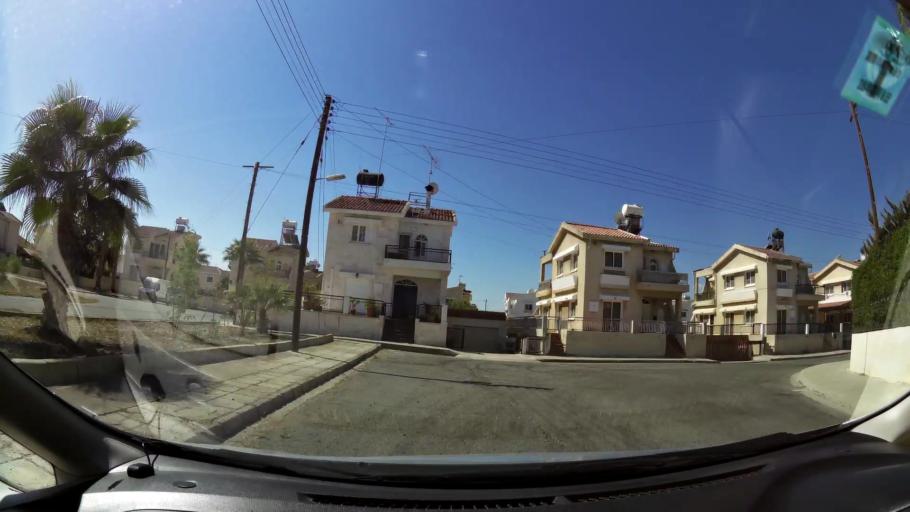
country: CY
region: Larnaka
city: Voroklini
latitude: 34.9606
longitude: 33.6538
